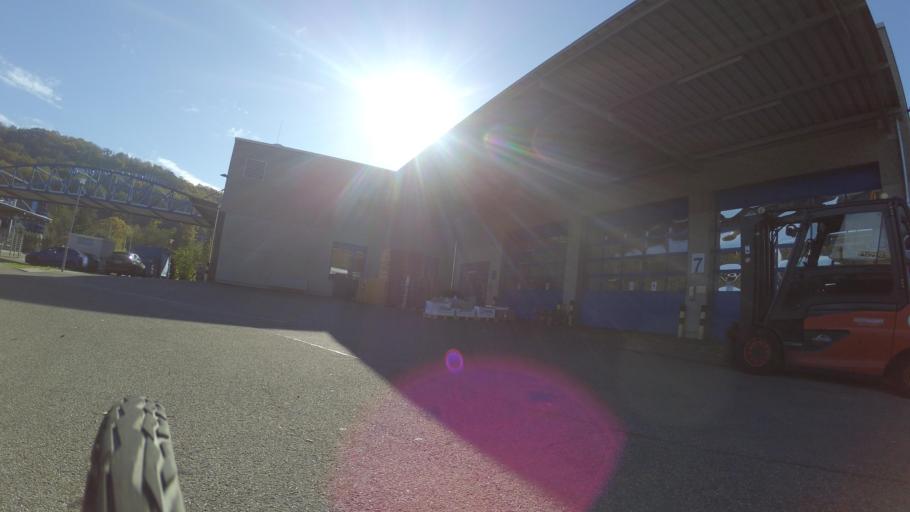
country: DE
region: Baden-Wuerttemberg
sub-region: Regierungsbezirk Stuttgart
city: Forchtenberg
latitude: 49.2921
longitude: 9.5715
